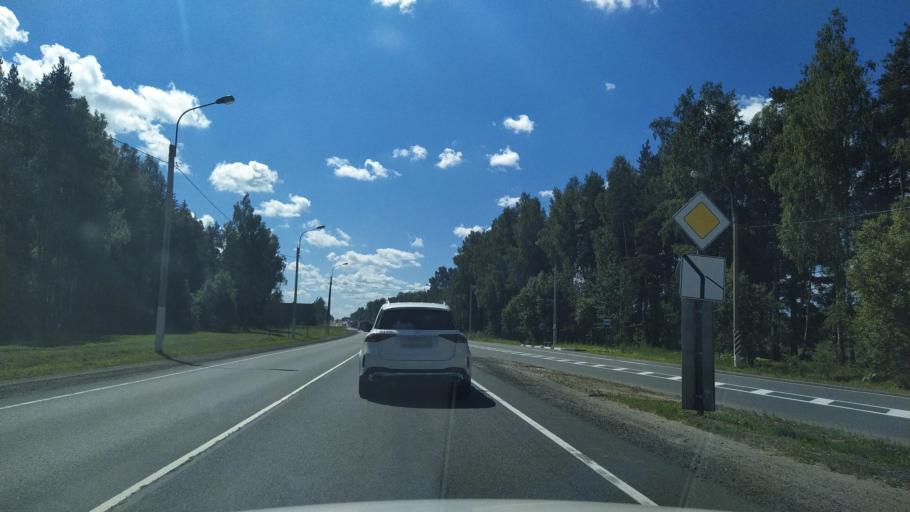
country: RU
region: Leningrad
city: Luga
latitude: 58.6241
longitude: 29.8331
